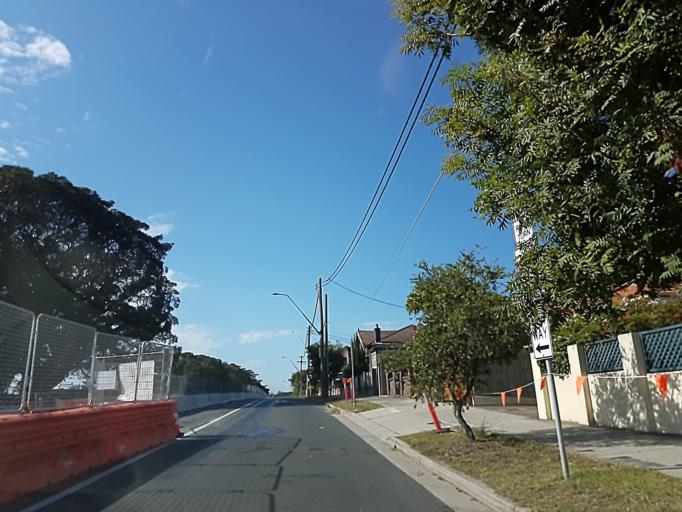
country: AU
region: New South Wales
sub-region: Randwick
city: Kingsford
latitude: -33.9155
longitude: 151.2350
